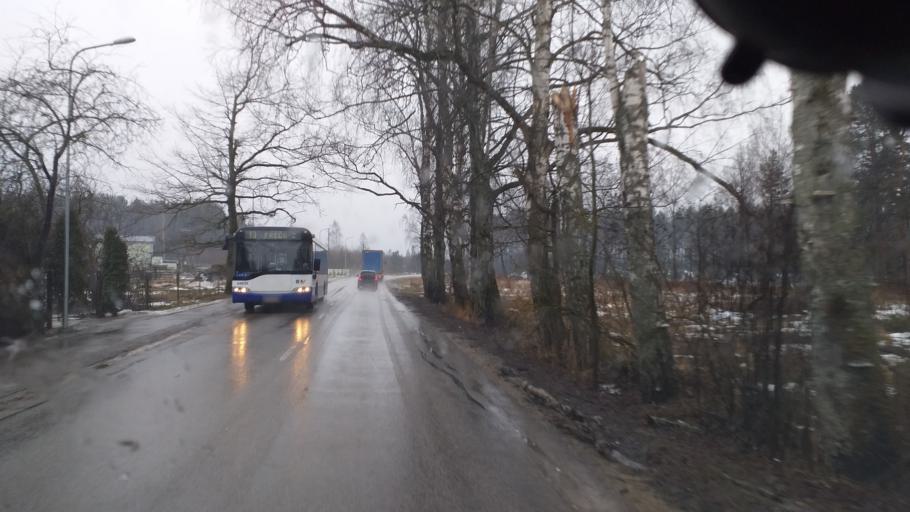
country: LV
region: Babite
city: Pinki
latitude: 56.9738
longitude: 23.9690
